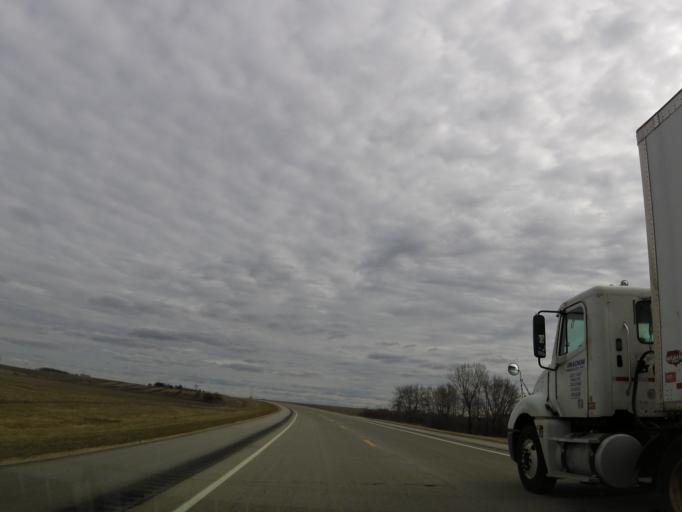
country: US
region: Minnesota
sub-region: Fillmore County
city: Spring Valley
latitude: 43.5569
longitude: -92.3861
